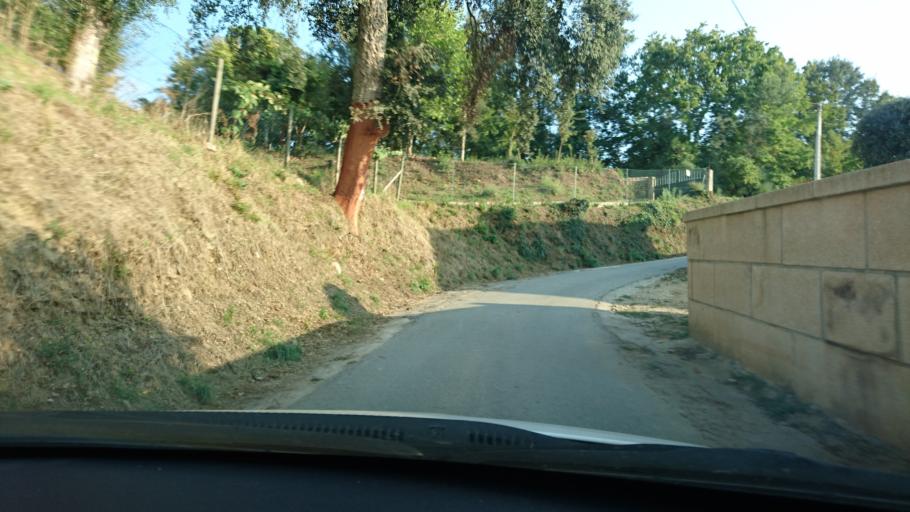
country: PT
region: Vila Real
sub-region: Mondim de Basto
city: Mondim de Basto
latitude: 41.4511
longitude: -7.9278
